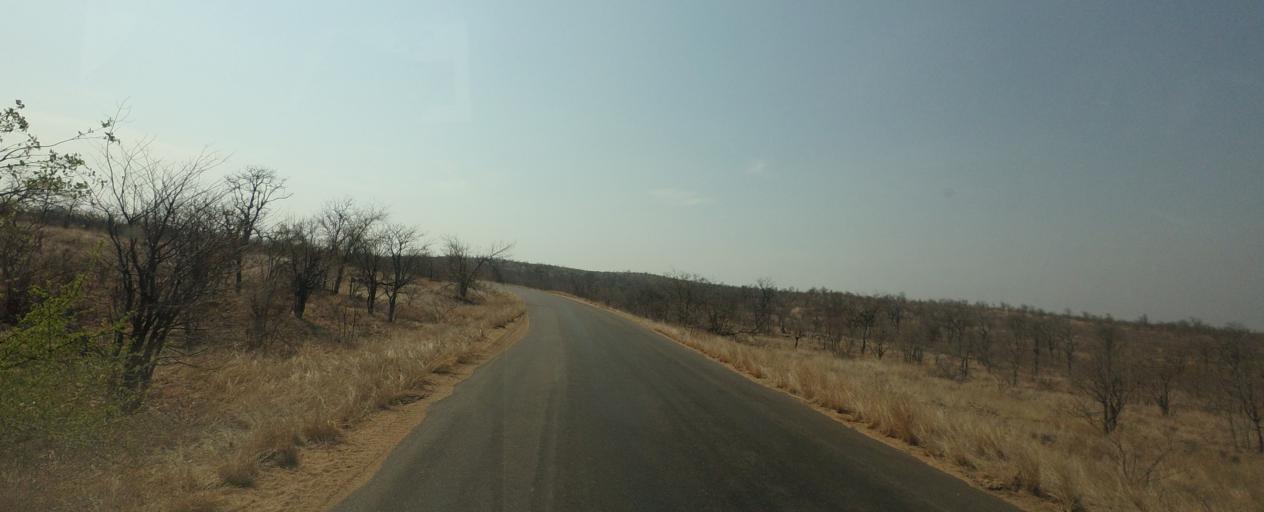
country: ZA
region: Limpopo
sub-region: Mopani District Municipality
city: Phalaborwa
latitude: -23.9726
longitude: 31.6346
